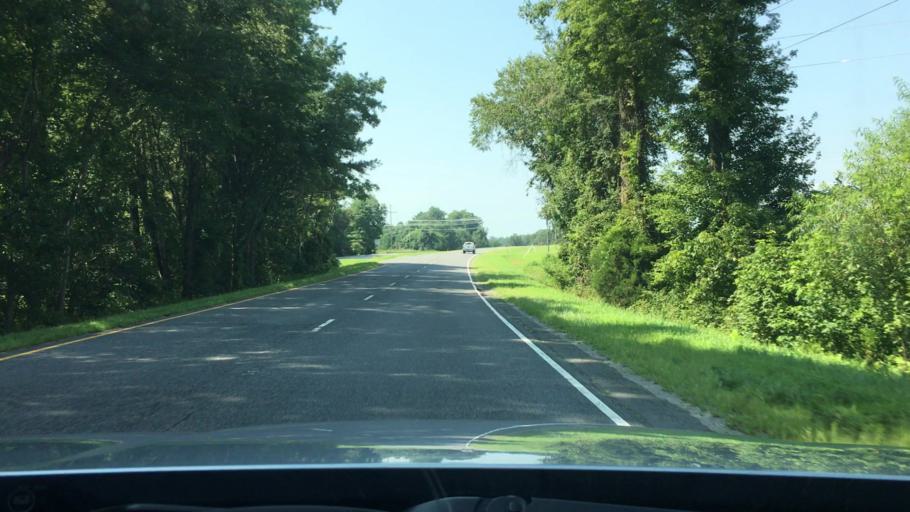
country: US
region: Virginia
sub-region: Caroline County
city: Bowling Green
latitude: 37.9796
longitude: -77.4222
